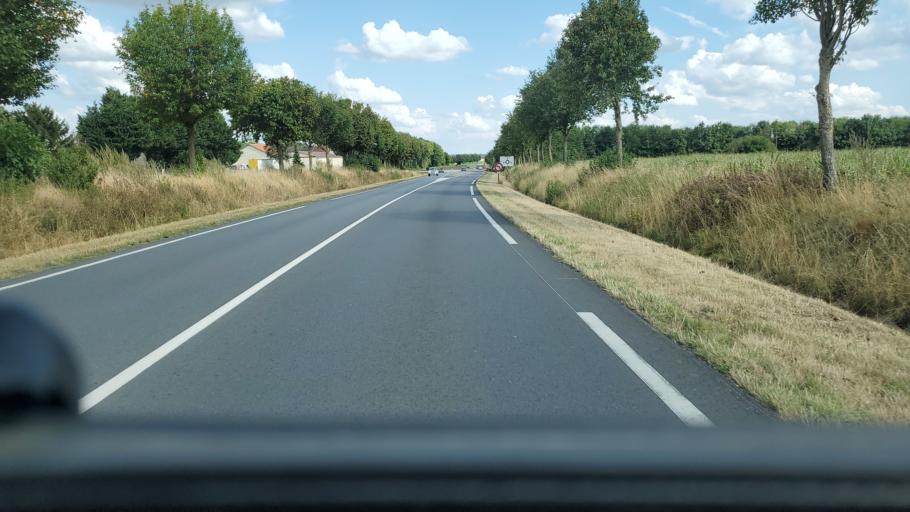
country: FR
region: Ile-de-France
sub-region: Departement de Seine-et-Marne
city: Nanteuil-les-Meaux
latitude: 48.9130
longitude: 2.9170
